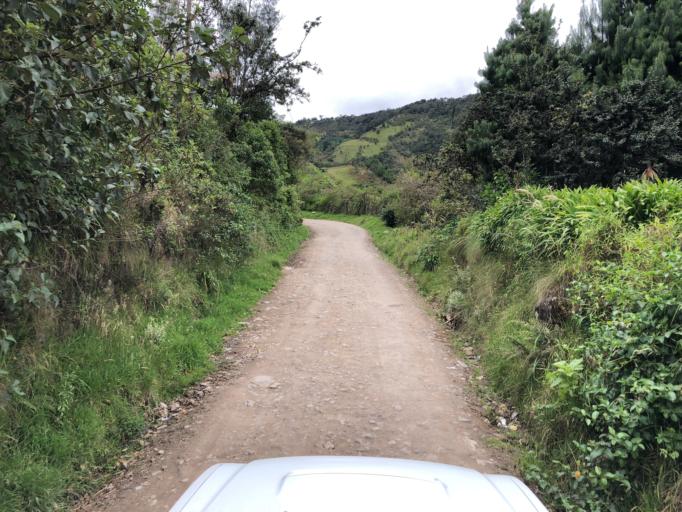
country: CO
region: Cauca
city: Totoro
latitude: 2.5091
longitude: -76.3693
